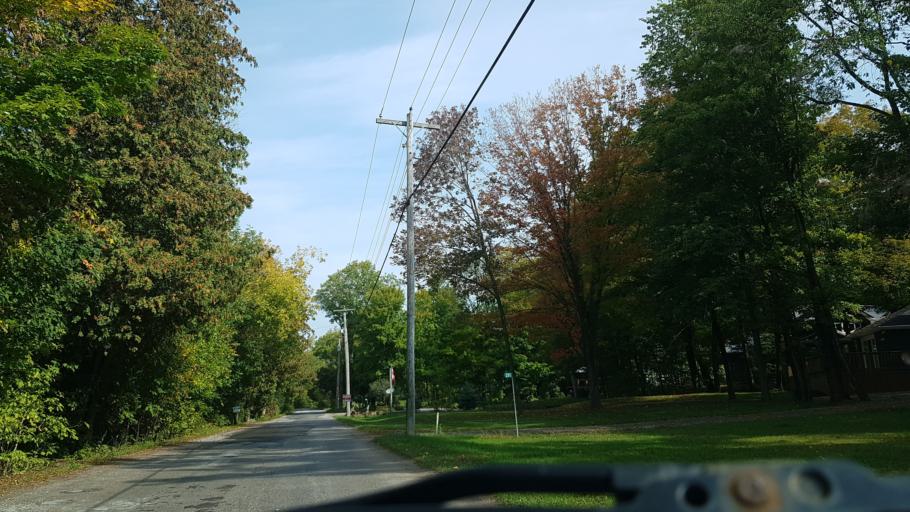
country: CA
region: Ontario
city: Orillia
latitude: 44.6626
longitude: -79.0993
